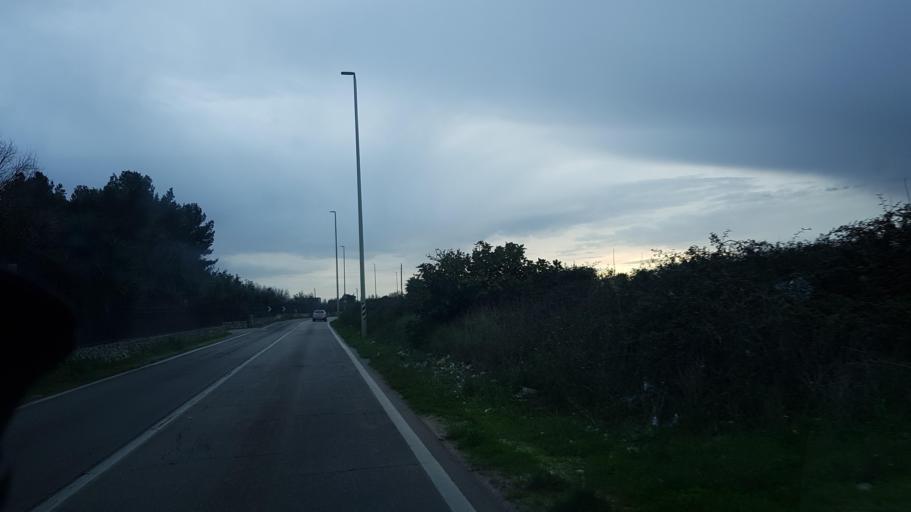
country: IT
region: Apulia
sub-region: Provincia di Lecce
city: Merine
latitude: 40.3244
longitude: 18.2235
